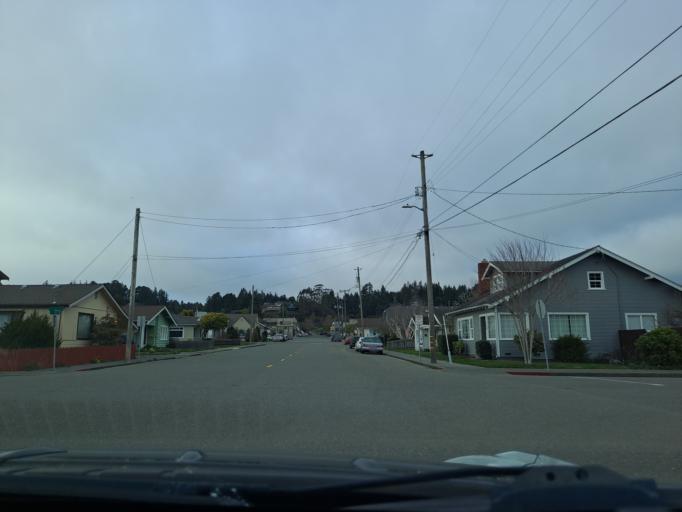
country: US
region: California
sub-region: Humboldt County
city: Fortuna
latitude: 40.5954
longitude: -124.1555
